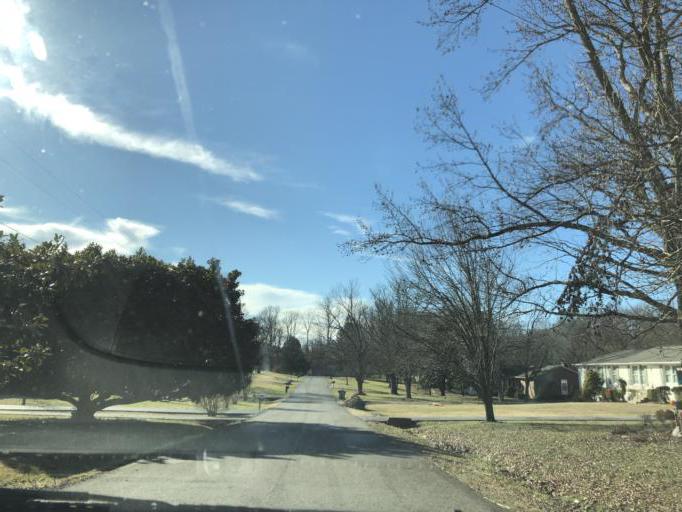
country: US
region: Tennessee
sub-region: Wilson County
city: Mount Juliet
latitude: 36.1812
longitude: -86.5266
